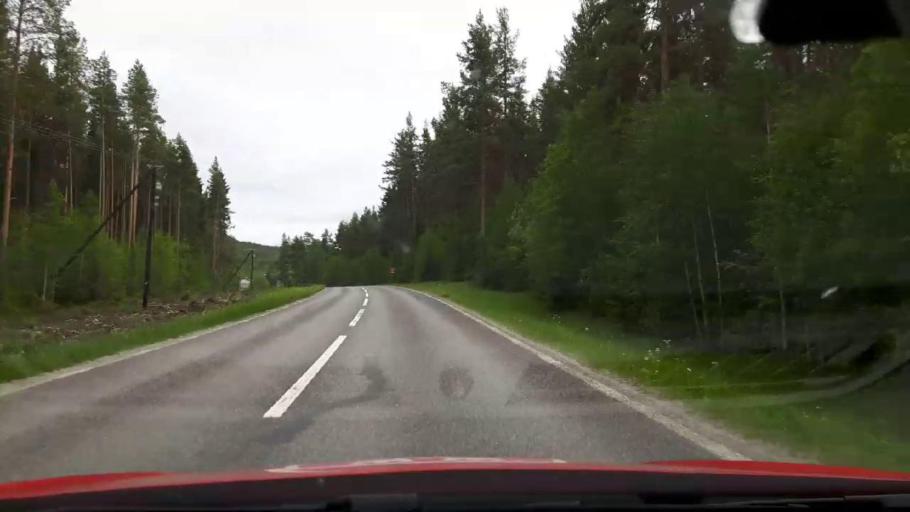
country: SE
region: Jaemtland
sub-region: Ragunda Kommun
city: Hammarstrand
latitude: 63.0646
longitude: 16.3905
